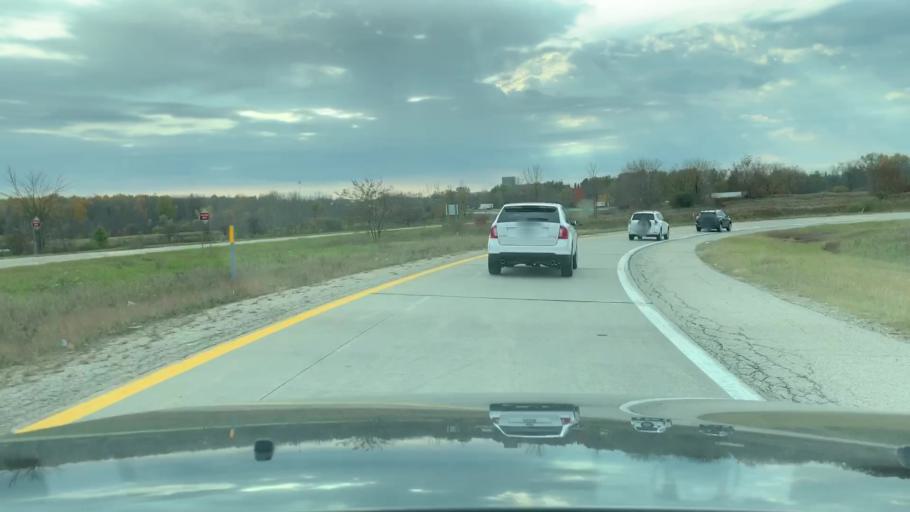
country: US
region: Michigan
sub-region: Ottawa County
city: Zeeland
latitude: 42.7822
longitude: -86.0252
